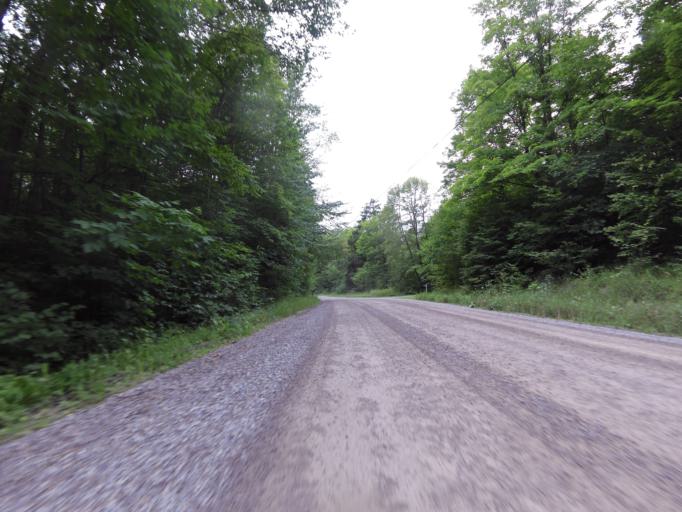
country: CA
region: Ontario
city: Carleton Place
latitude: 45.1572
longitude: -76.2426
